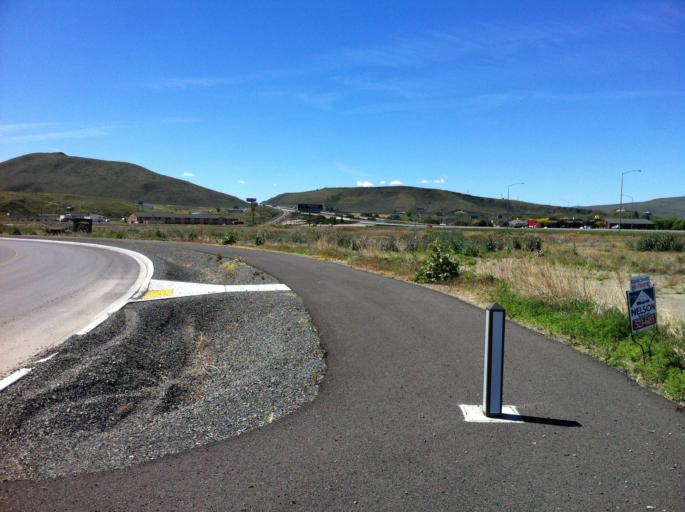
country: US
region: Oregon
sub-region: Baker County
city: Baker City
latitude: 44.7888
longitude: -117.8096
